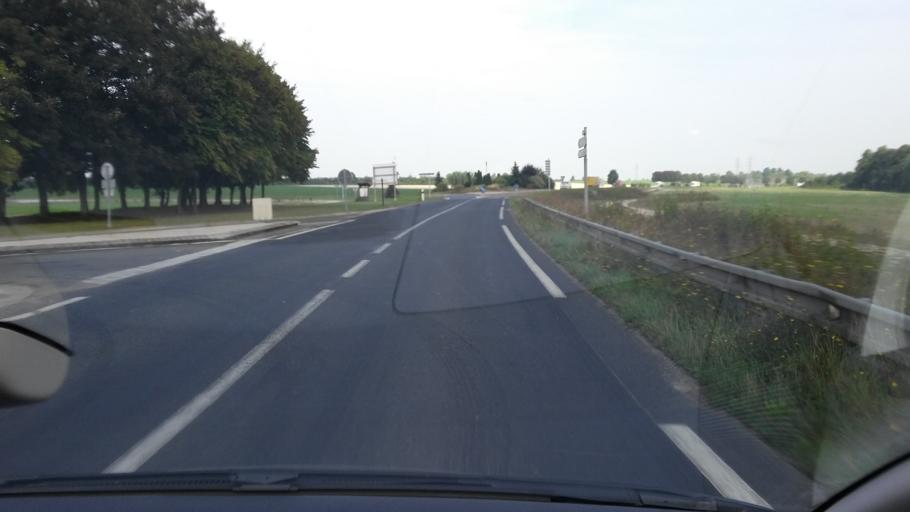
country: FR
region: Champagne-Ardenne
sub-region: Departement de la Marne
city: Fere-Champenoise
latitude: 48.7604
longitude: 3.9999
